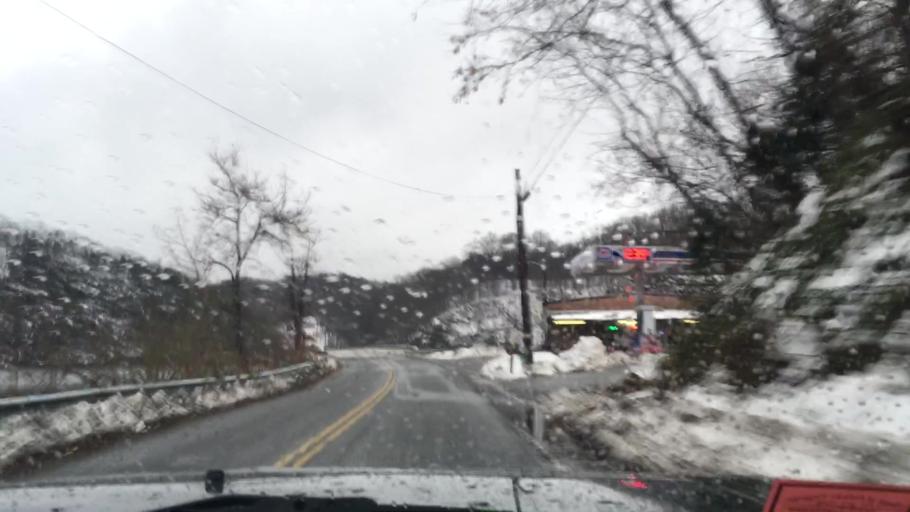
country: US
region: Virginia
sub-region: Pulaski County
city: Dublin
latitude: 37.0044
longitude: -80.6848
